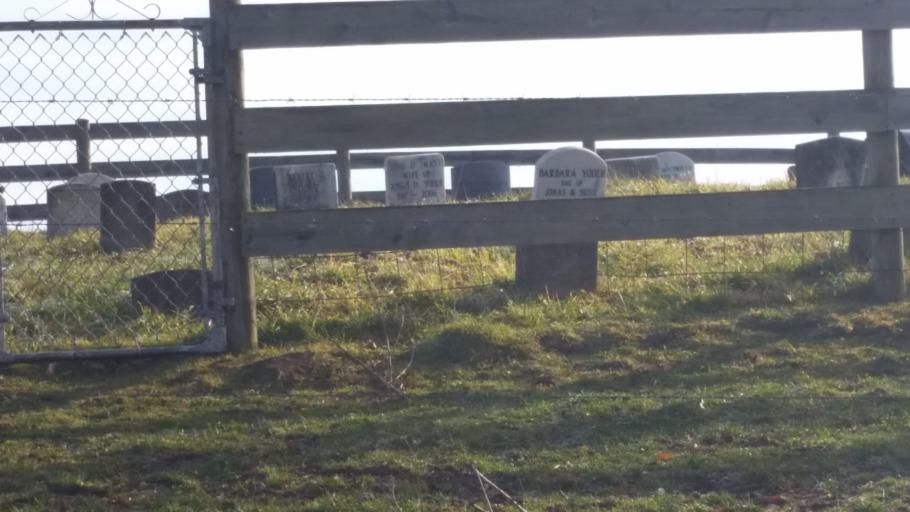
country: US
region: Ohio
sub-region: Wayne County
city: Apple Creek
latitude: 40.7330
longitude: -81.7752
